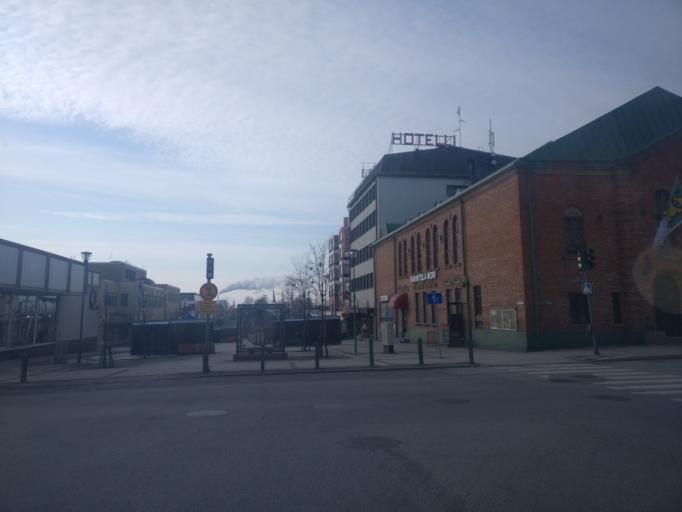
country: FI
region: Lapland
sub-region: Kemi-Tornio
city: Kemi
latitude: 65.7369
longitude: 24.5664
